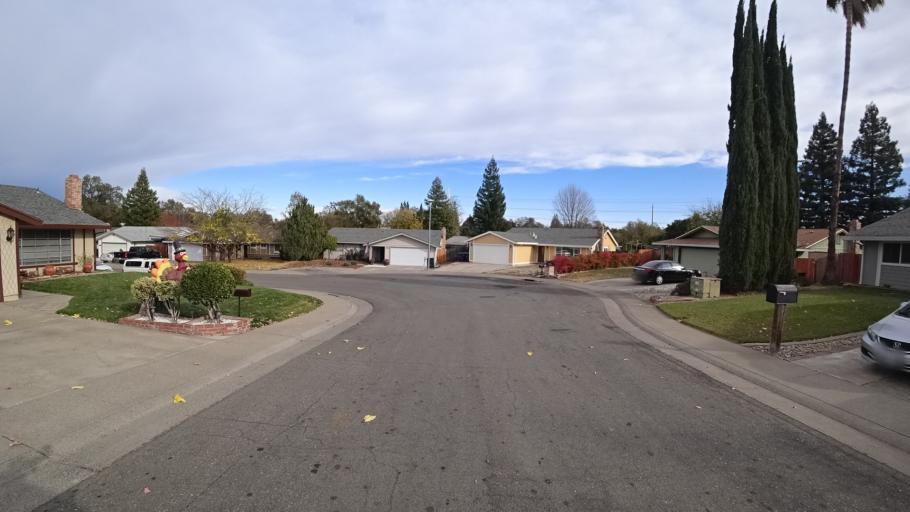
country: US
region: California
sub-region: Sacramento County
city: Citrus Heights
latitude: 38.7083
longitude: -121.2512
